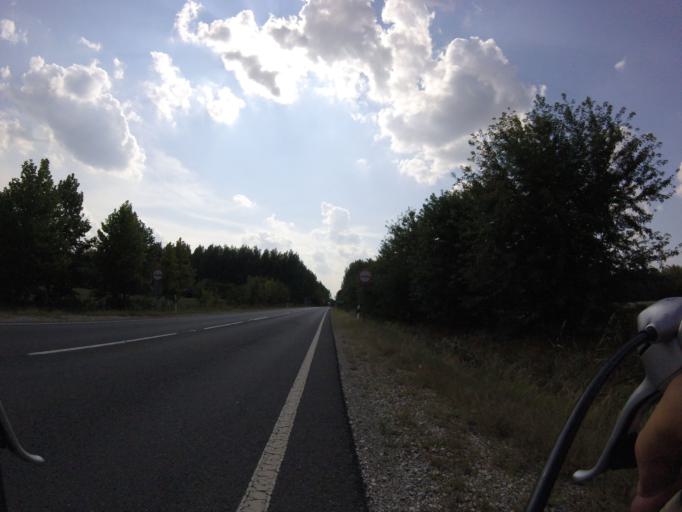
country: HU
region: Szabolcs-Szatmar-Bereg
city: Demecser
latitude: 48.0729
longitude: 21.9594
